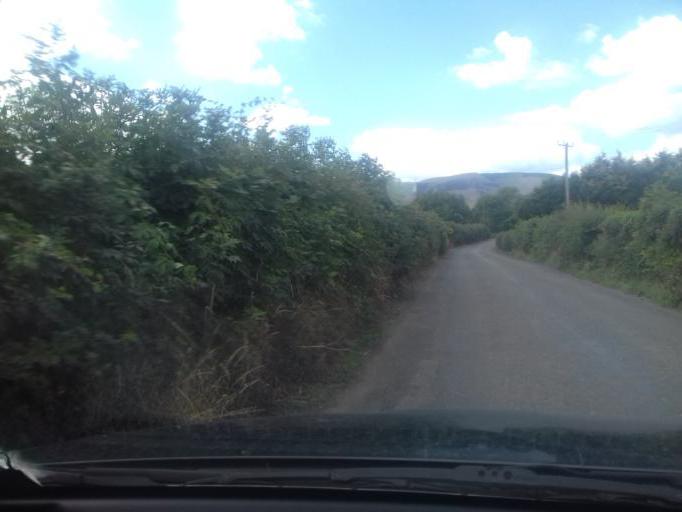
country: IE
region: Munster
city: Carrick-on-Suir
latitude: 52.2211
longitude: -7.4511
